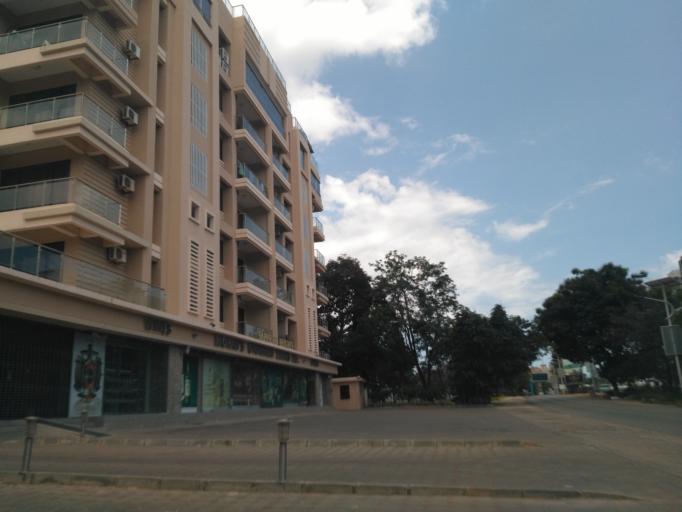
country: TZ
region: Dar es Salaam
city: Magomeni
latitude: -6.7725
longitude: 39.2760
